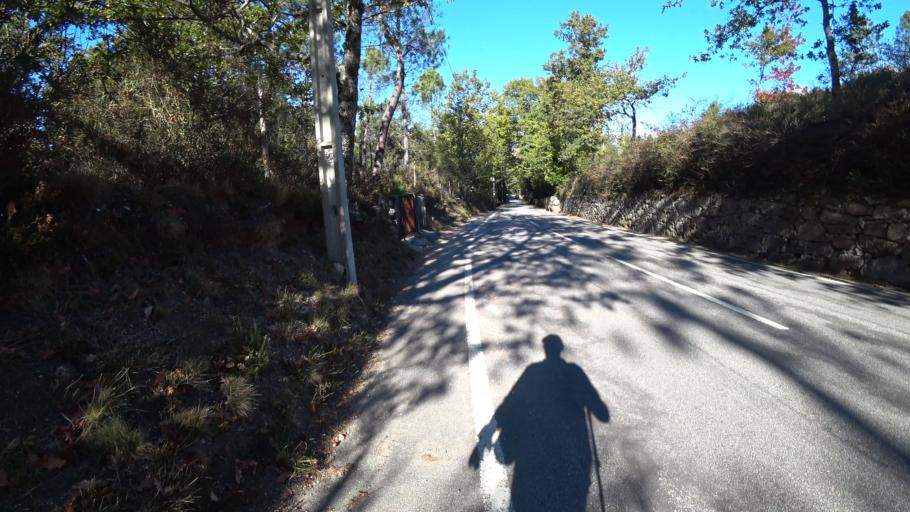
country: PT
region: Braga
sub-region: Vieira do Minho
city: Real
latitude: 41.7536
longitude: -8.1939
